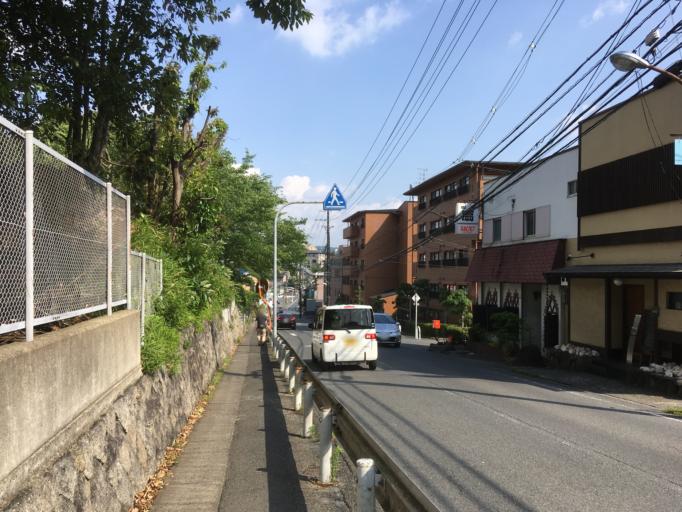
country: JP
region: Nara
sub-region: Ikoma-shi
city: Ikoma
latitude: 34.6880
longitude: 135.7000
